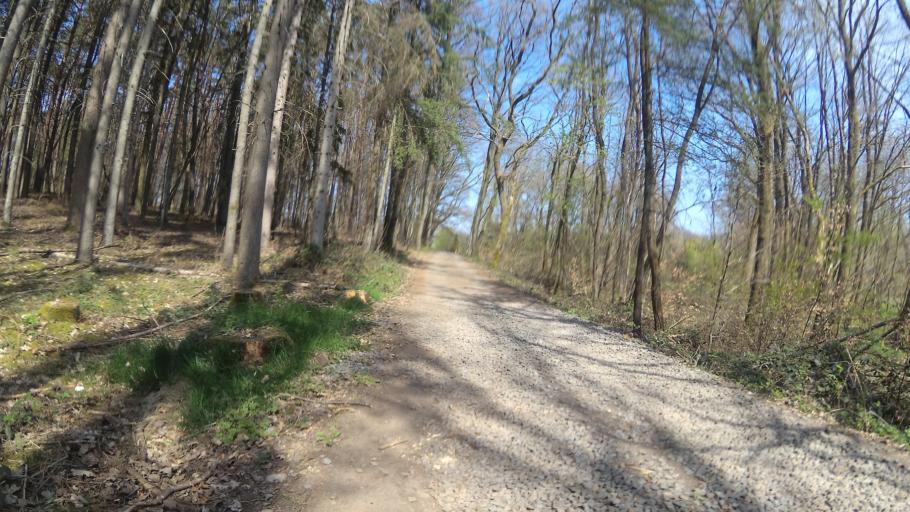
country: DE
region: Rheinland-Pfalz
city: Waldmohr
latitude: 49.3879
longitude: 7.3496
